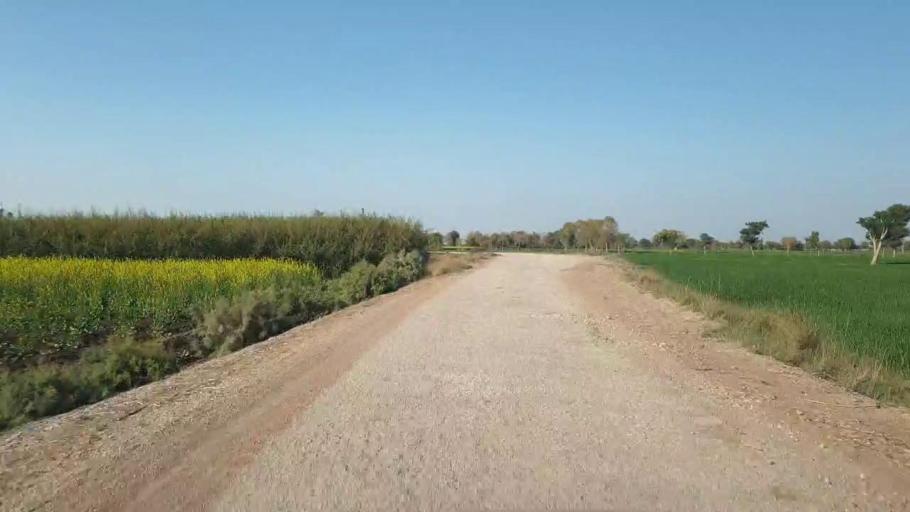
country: PK
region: Sindh
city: Shahpur Chakar
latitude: 26.1783
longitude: 68.6751
